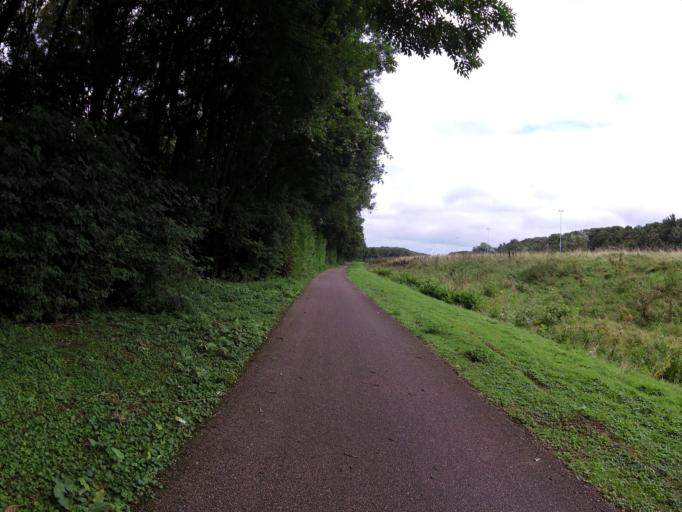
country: NL
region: Gelderland
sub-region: Gemeente Maasdriel
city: Hedel
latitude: 51.7041
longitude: 5.2557
